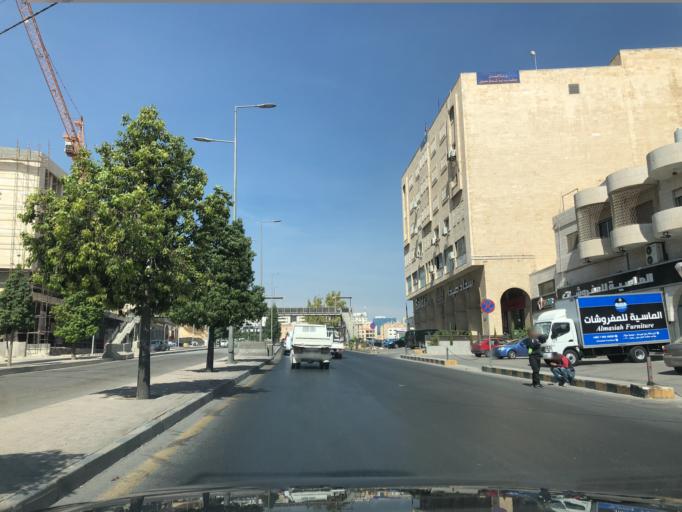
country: JO
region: Amman
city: Al Jubayhah
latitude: 32.0219
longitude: 35.8611
